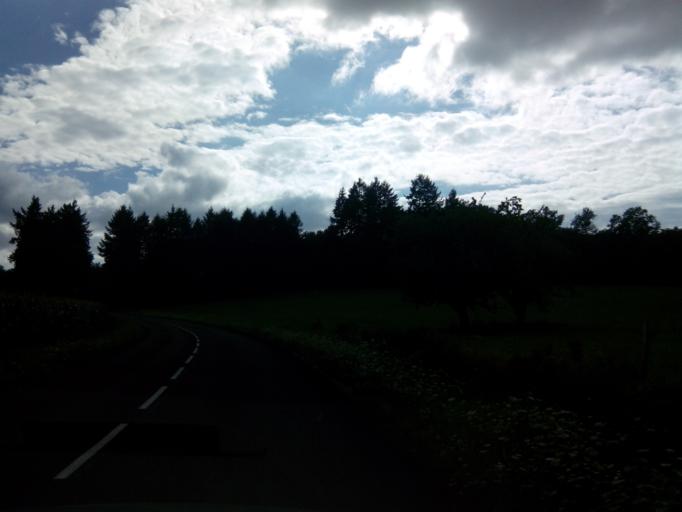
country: FR
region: Limousin
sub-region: Departement de la Haute-Vienne
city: Saint-Leonard-de-Noblat
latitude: 45.8330
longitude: 1.5512
